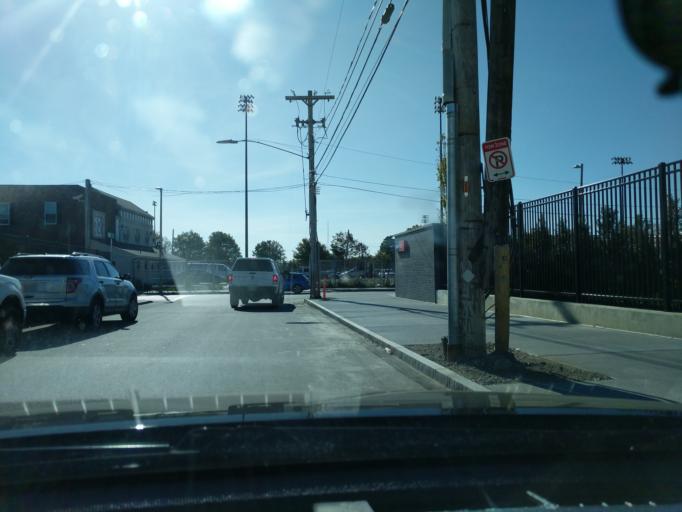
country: US
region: Massachusetts
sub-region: Suffolk County
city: South Boston
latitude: 42.3278
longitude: -71.0694
